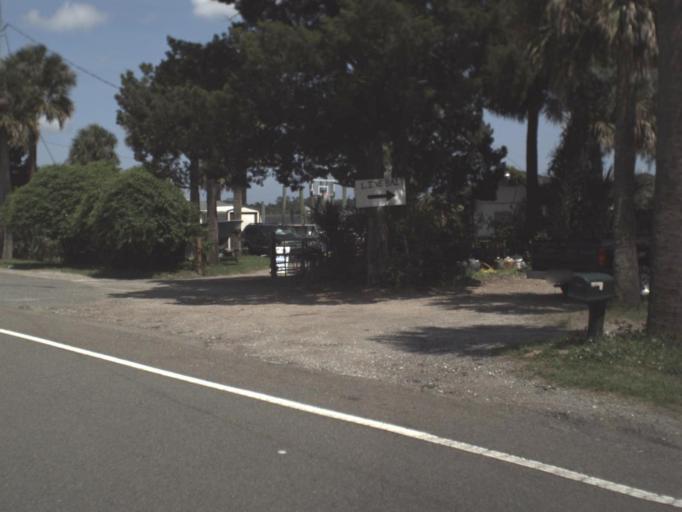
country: US
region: Florida
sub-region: Duval County
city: Jacksonville
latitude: 30.4160
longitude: -81.5415
